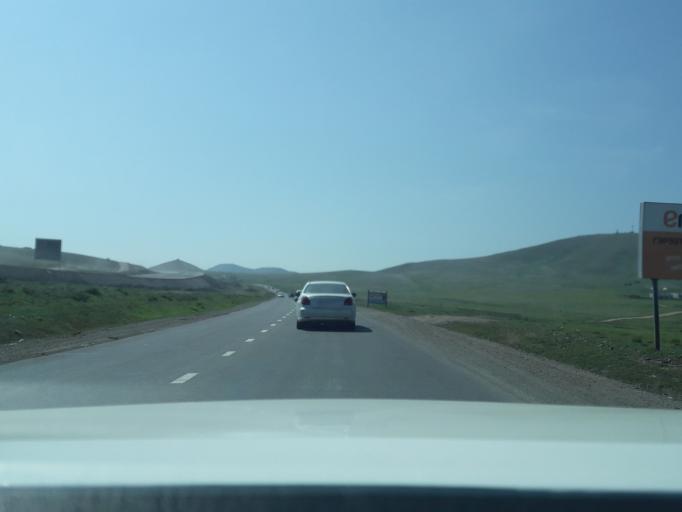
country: MN
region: Ulaanbaatar
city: Ulaanbaatar
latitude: 47.8003
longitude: 106.7465
